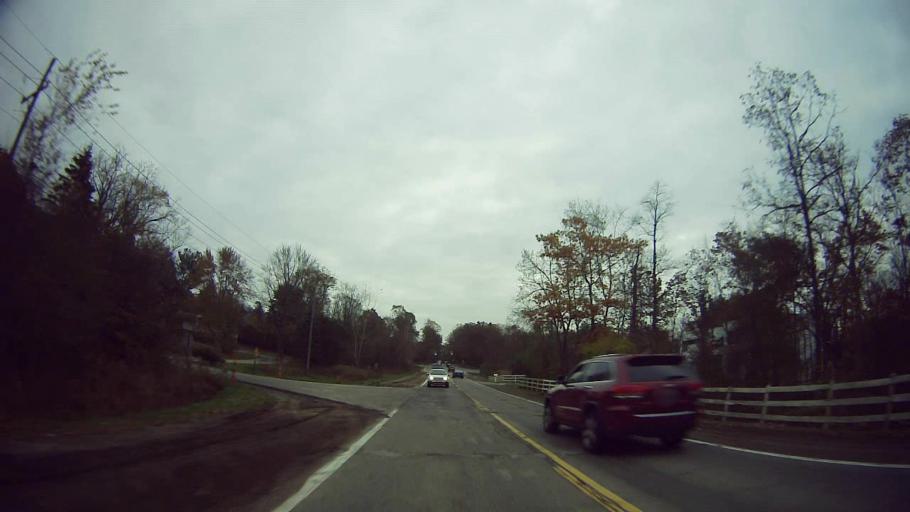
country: US
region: Michigan
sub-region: Oakland County
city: Franklin
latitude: 42.5151
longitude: -83.3065
